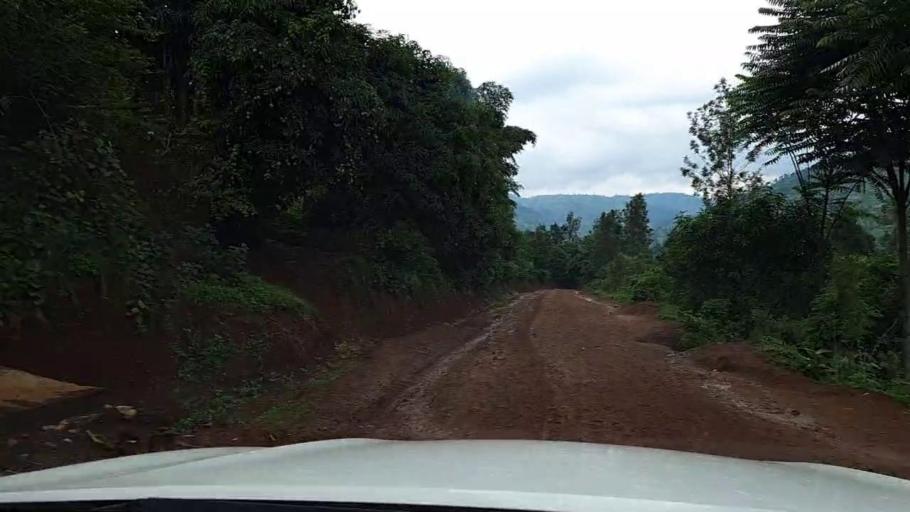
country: RW
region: Western Province
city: Cyangugu
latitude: -2.5690
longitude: 29.0328
